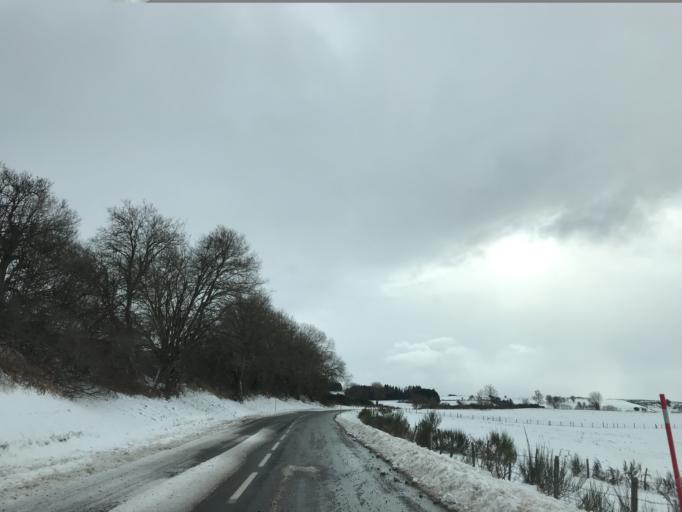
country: FR
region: Auvergne
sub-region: Departement du Puy-de-Dome
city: Aydat
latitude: 45.6816
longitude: 2.9366
